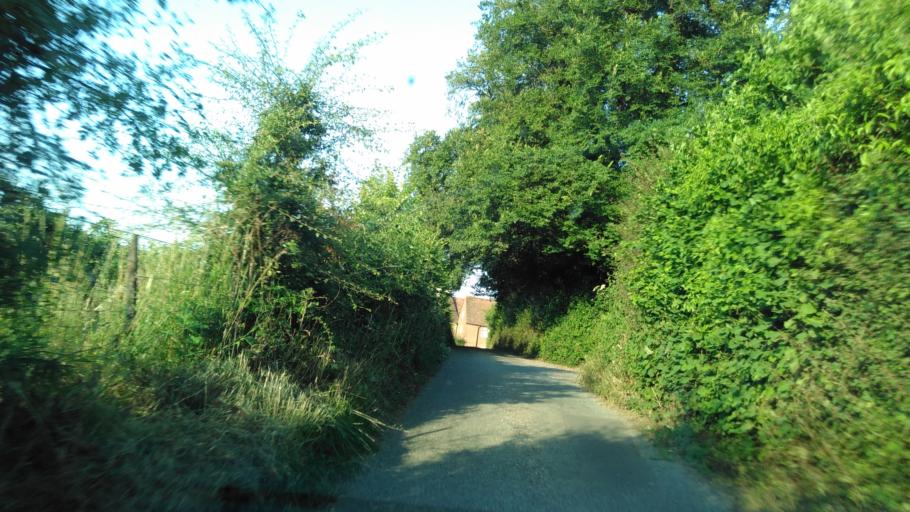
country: GB
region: England
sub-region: Kent
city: Chartham
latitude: 51.2671
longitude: 1.0124
